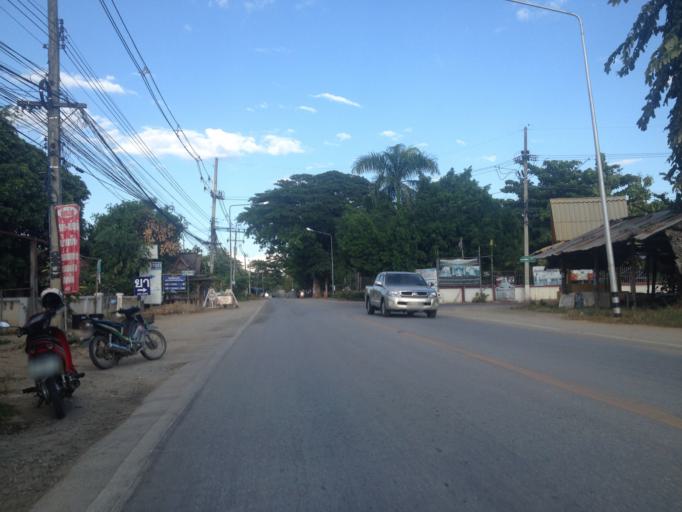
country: TH
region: Chiang Mai
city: San Pa Tong
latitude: 18.6131
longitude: 98.8551
